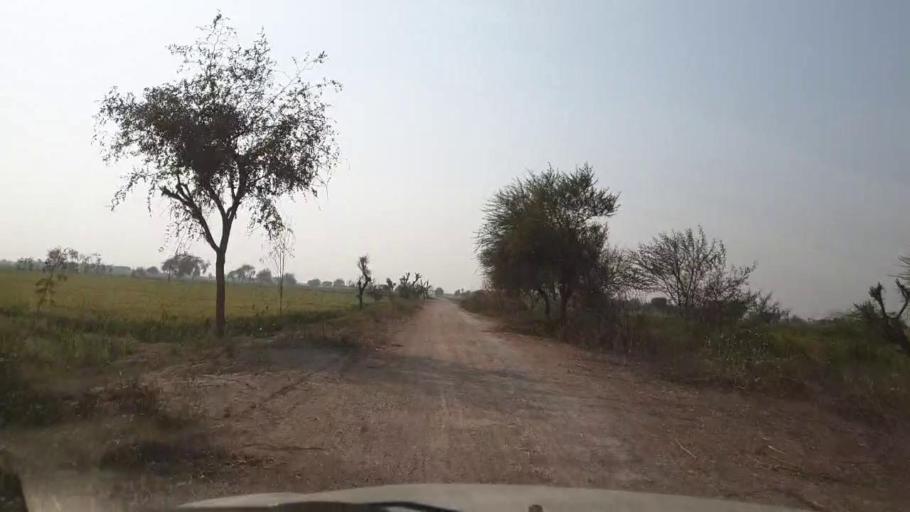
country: PK
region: Sindh
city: Pithoro
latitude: 25.6872
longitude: 69.2127
